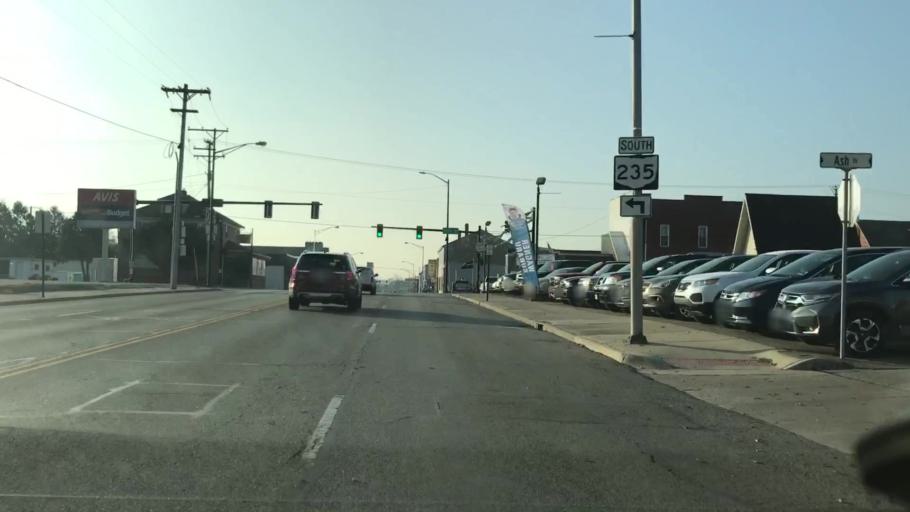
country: US
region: Ohio
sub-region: Greene County
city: Fairborn
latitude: 39.8259
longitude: -84.0274
